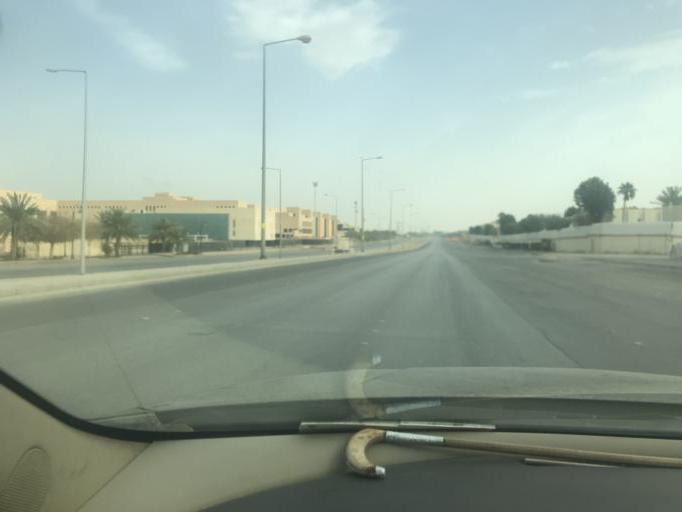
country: SA
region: Ar Riyad
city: Riyadh
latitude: 24.8133
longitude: 46.6899
